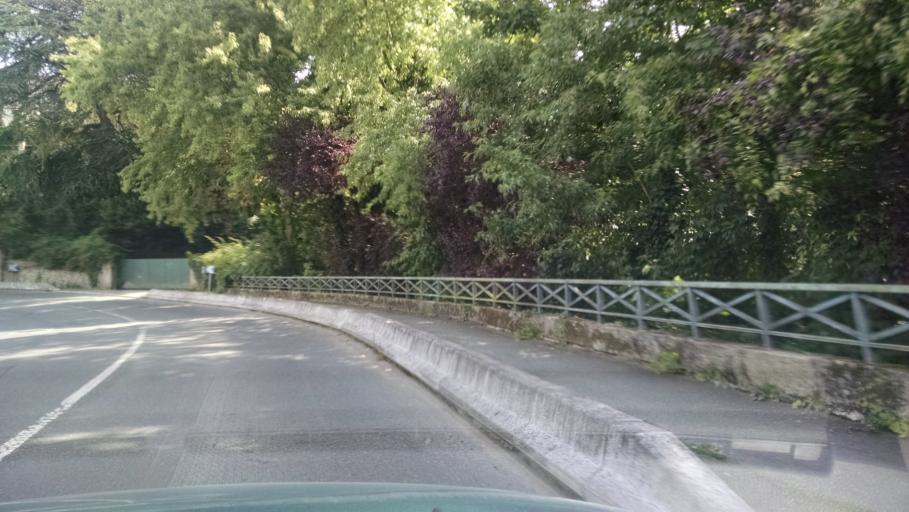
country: FR
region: Pays de la Loire
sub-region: Departement de la Loire-Atlantique
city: Clisson
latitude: 47.0906
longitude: -1.2815
